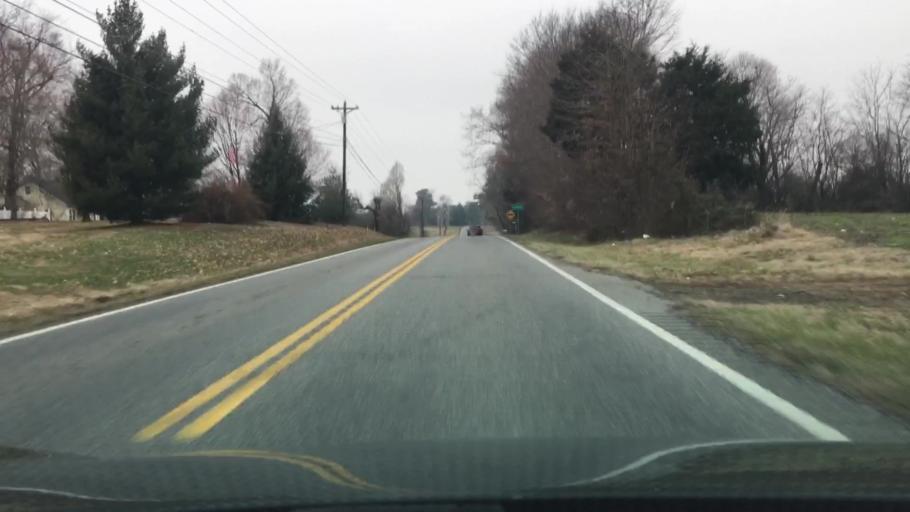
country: US
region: Kentucky
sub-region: Livingston County
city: Ledbetter
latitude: 36.9667
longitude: -88.4464
